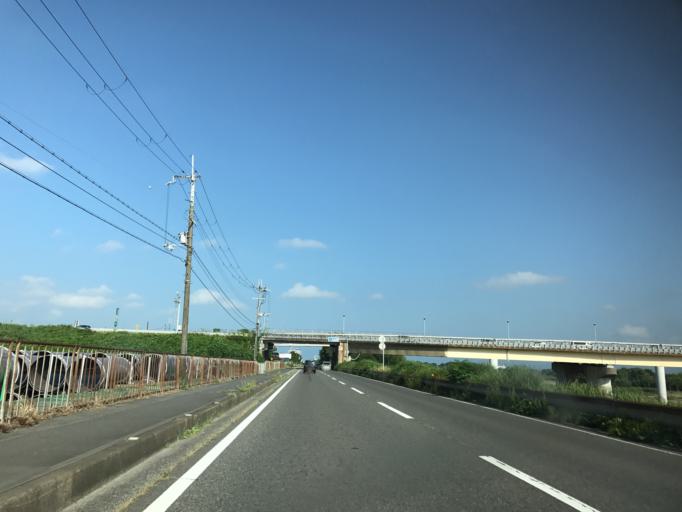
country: JP
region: Shiga Prefecture
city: Moriyama
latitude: 35.0250
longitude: 136.0395
